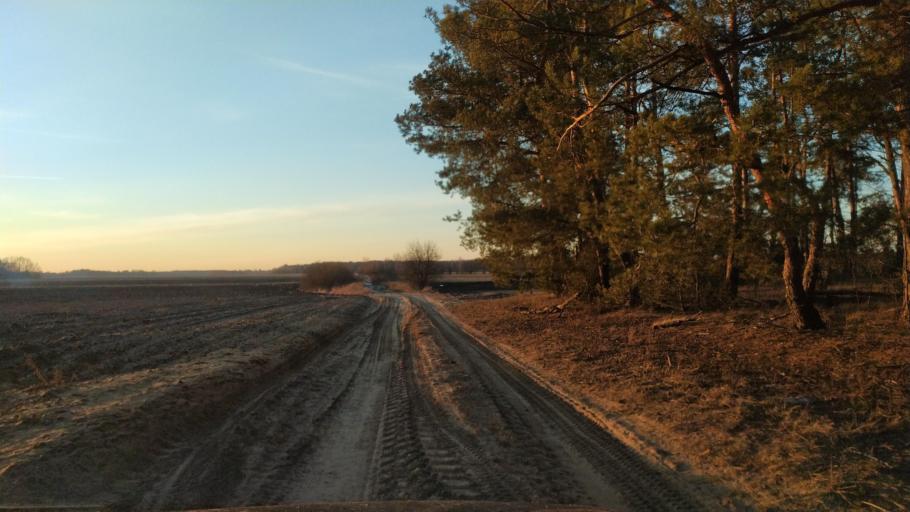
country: BY
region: Brest
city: Pruzhany
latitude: 52.5527
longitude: 24.2671
